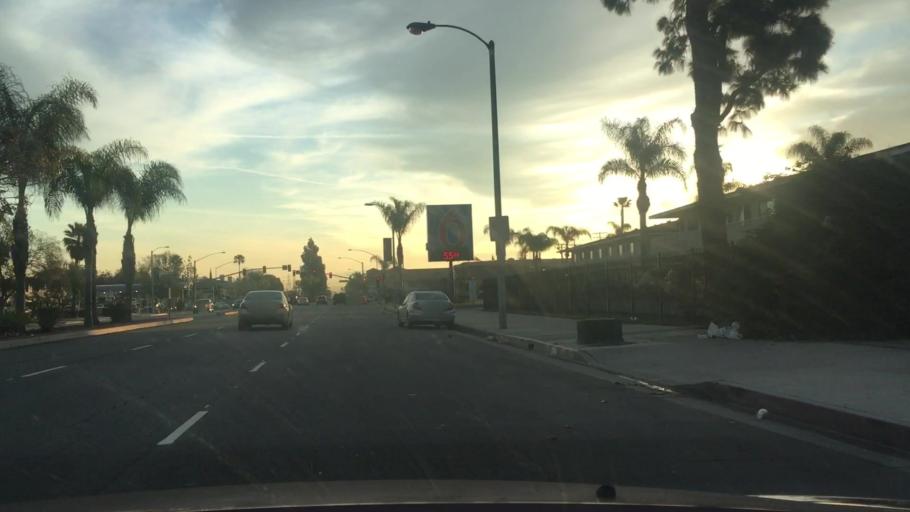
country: US
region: California
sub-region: Orange County
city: Stanton
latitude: 33.8027
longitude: -118.0039
